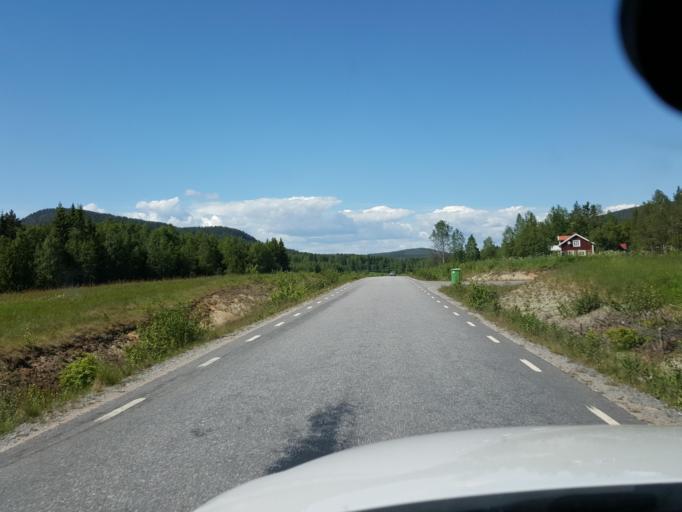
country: SE
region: Gaevleborg
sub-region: Ljusdals Kommun
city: Jaervsoe
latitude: 61.7192
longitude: 16.2920
